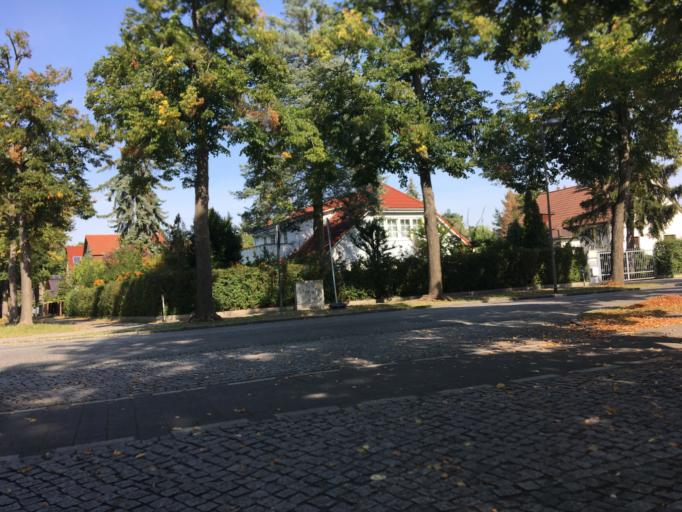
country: DE
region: Brandenburg
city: Zeuthen
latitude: 52.3684
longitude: 13.6295
